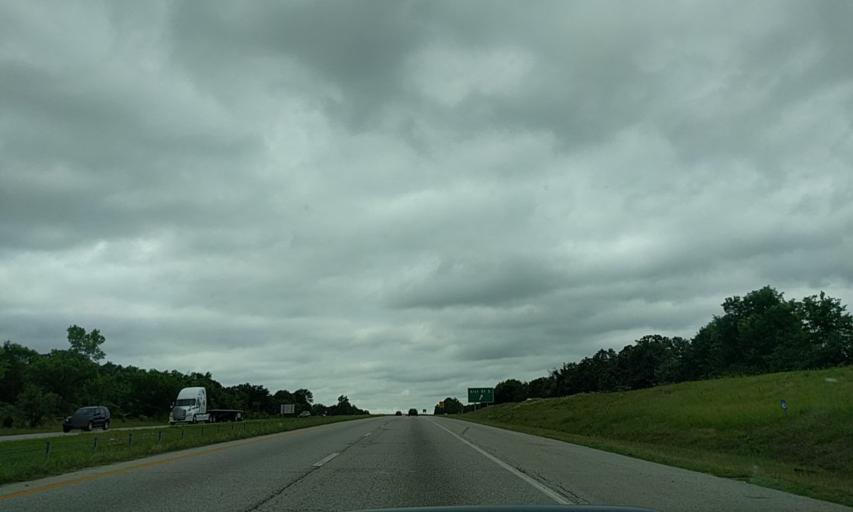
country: US
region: Oklahoma
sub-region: Tulsa County
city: Oakhurst
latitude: 36.0808
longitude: -96.0068
